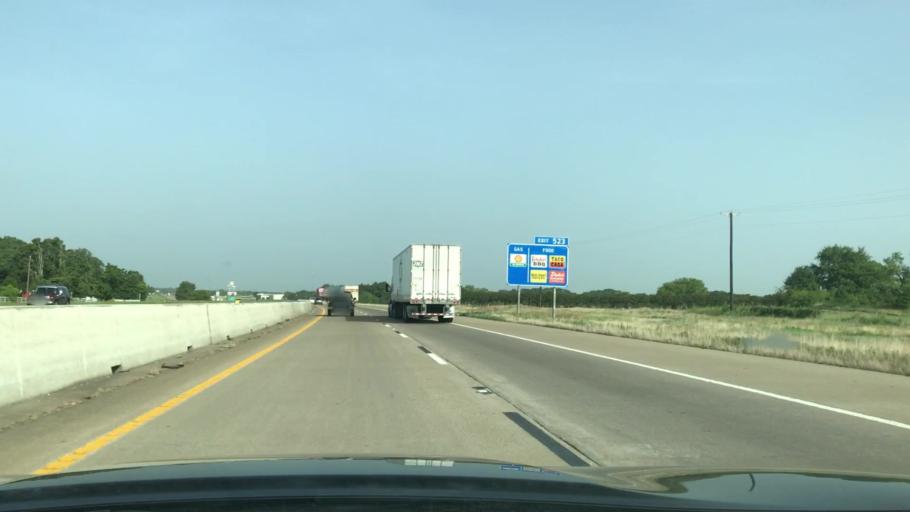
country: US
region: Texas
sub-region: Van Zandt County
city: Canton
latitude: 32.5980
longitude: -95.9036
